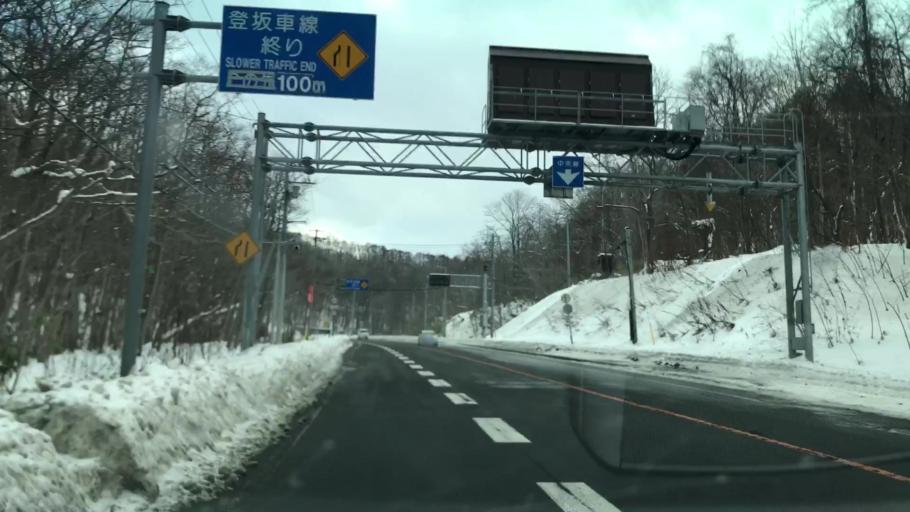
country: JP
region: Hokkaido
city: Yoichi
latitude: 43.2234
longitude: 140.7353
